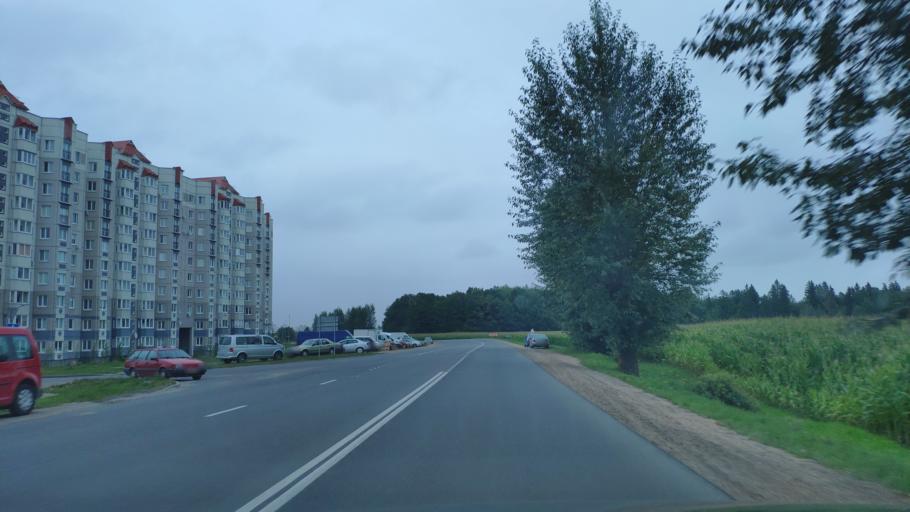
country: BY
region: Minsk
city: Azyartso
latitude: 53.8419
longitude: 27.4031
